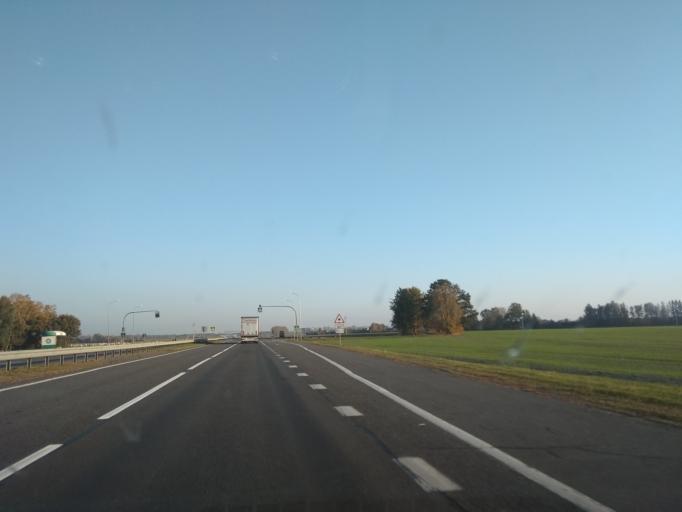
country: BY
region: Brest
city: Kobryn
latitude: 52.1952
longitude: 24.3029
